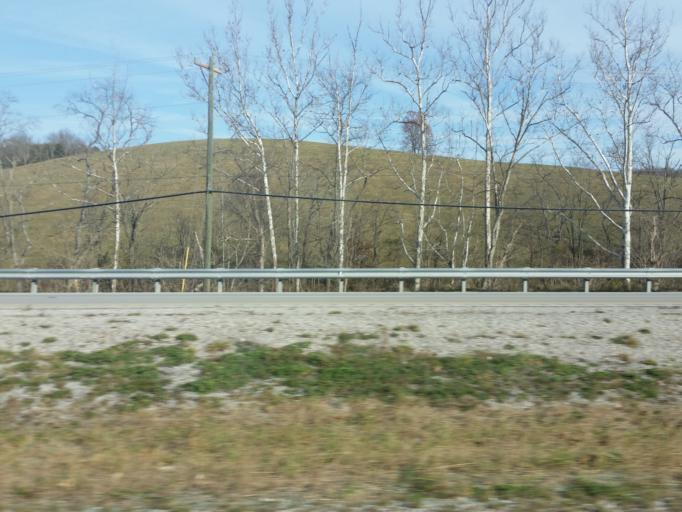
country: US
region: Kentucky
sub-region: Campbell County
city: Claryville
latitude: 38.8677
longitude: -84.3947
